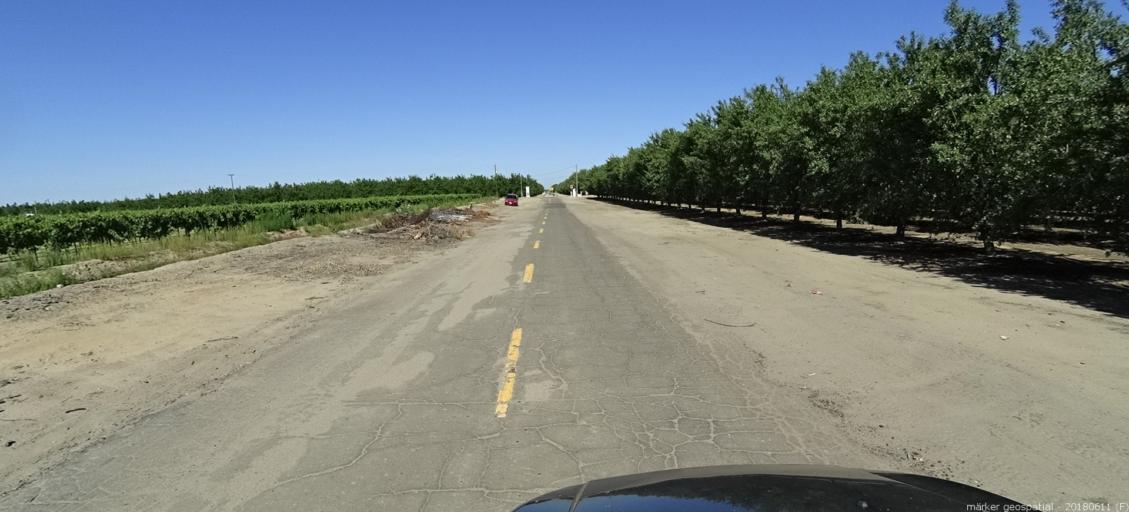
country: US
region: California
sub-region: Madera County
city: Madera
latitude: 36.9456
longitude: -120.1448
